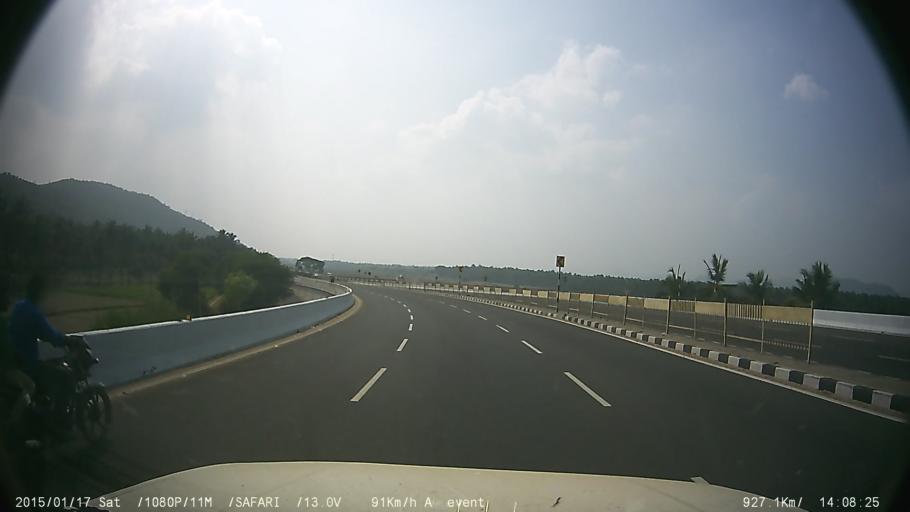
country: IN
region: Tamil Nadu
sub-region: Vellore
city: Ambur
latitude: 12.8263
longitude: 78.7620
